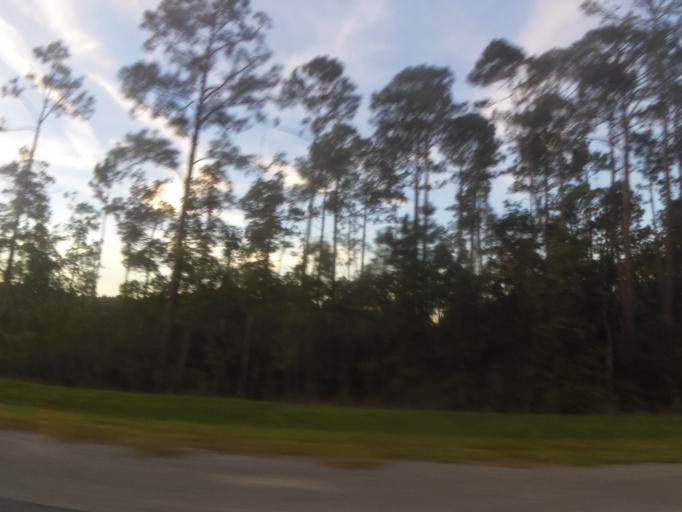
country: US
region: Florida
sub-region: Saint Johns County
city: Palm Valley
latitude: 30.1062
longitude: -81.4775
